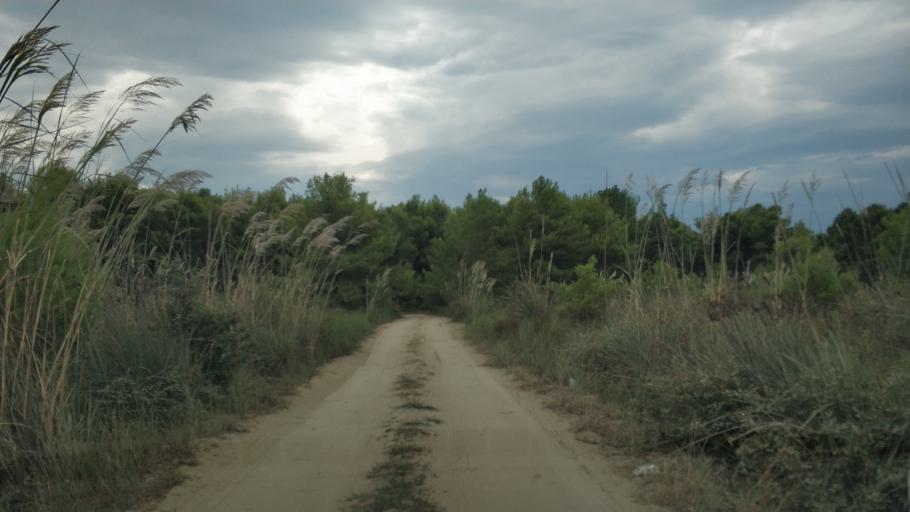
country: AL
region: Vlore
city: Vlore
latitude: 40.5035
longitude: 19.4196
